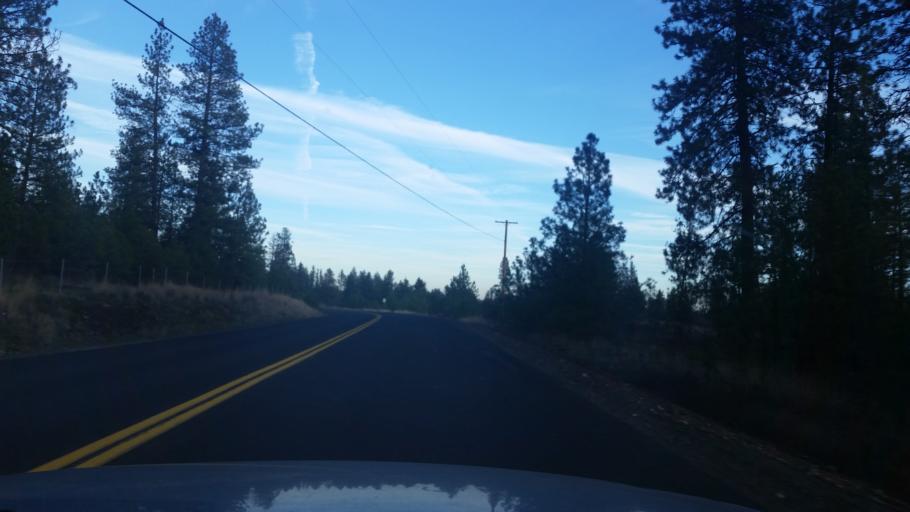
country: US
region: Washington
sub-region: Spokane County
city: Cheney
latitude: 47.4802
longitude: -117.5207
